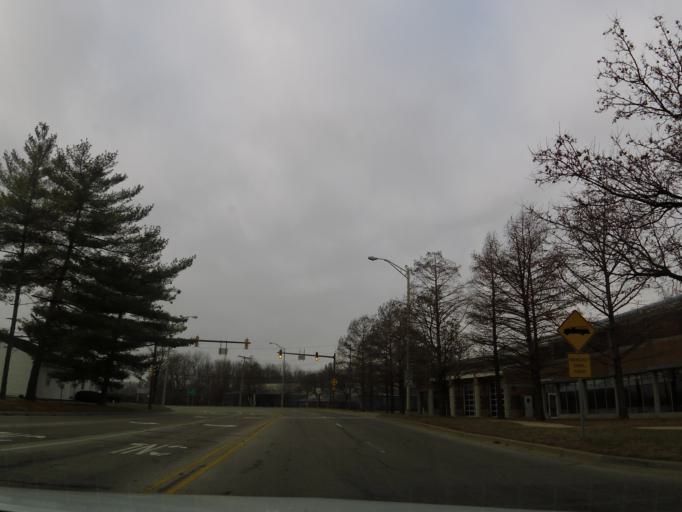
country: US
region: Indiana
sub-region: Bartholomew County
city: Columbus
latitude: 39.2094
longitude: -85.9216
